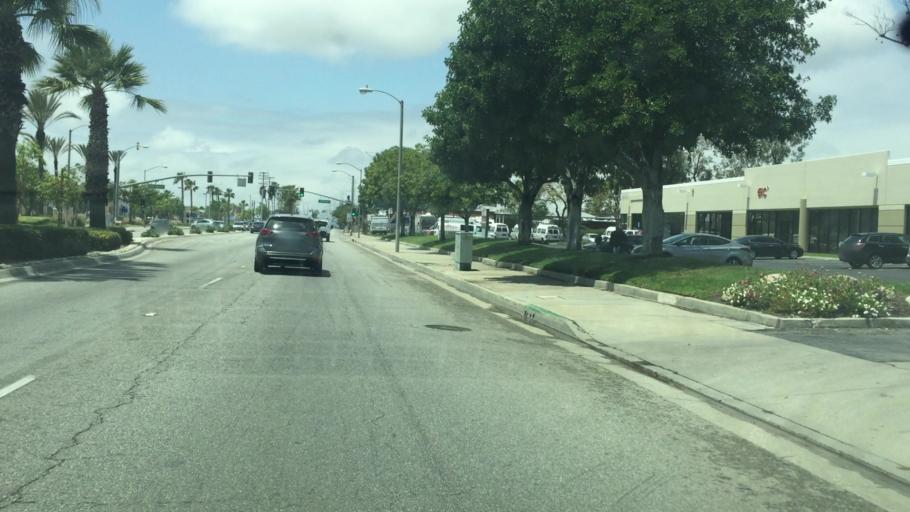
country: US
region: California
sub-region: Los Angeles County
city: Irwindale
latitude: 34.1071
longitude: -117.9373
